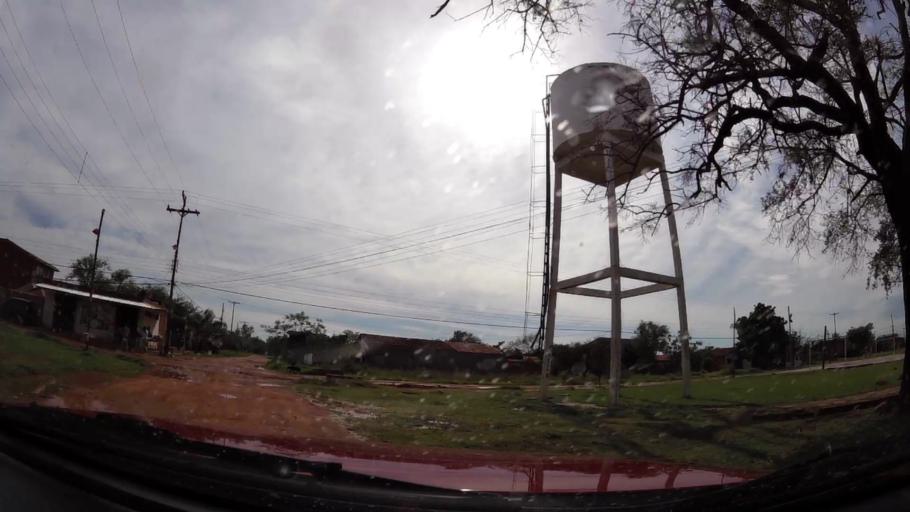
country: PY
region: Central
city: Limpio
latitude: -25.1794
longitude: -57.4946
